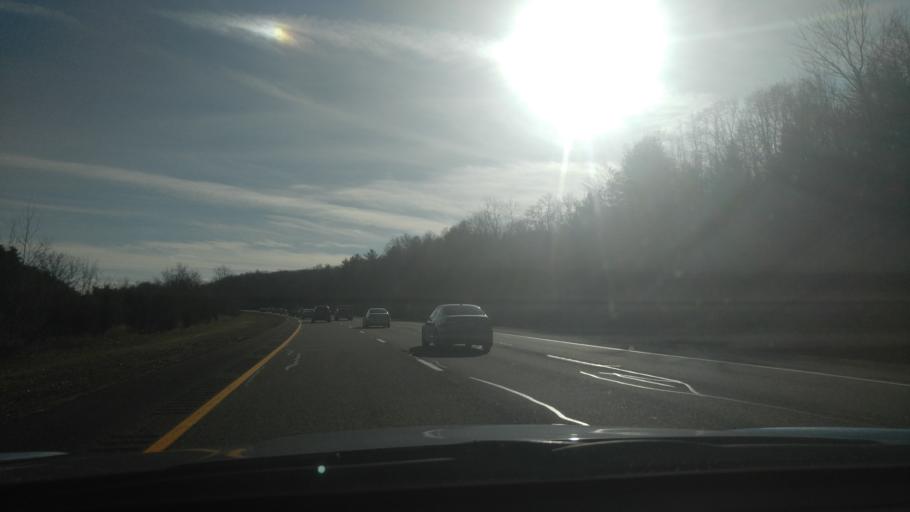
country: US
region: Rhode Island
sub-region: Providence County
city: Smithfield
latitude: 41.8959
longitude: -71.5236
